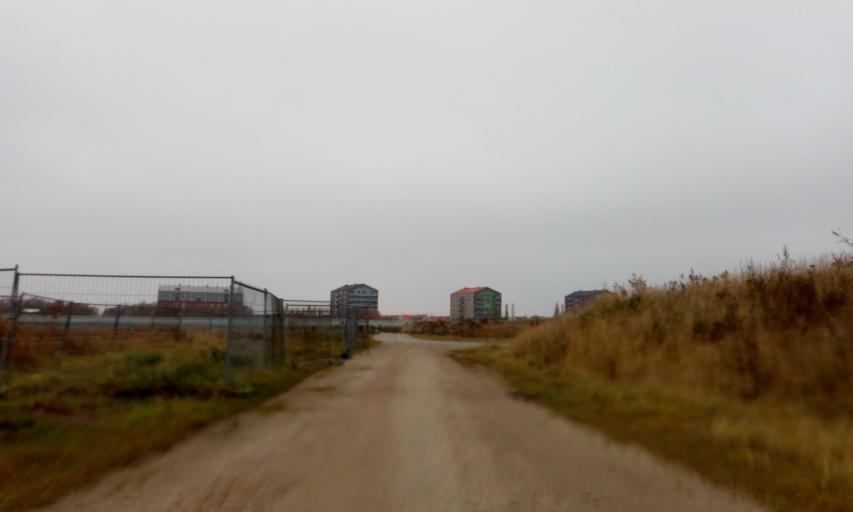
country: NL
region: South Holland
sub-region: Gemeente Lansingerland
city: Berkel en Rodenrijs
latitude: 51.9833
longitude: 4.4798
